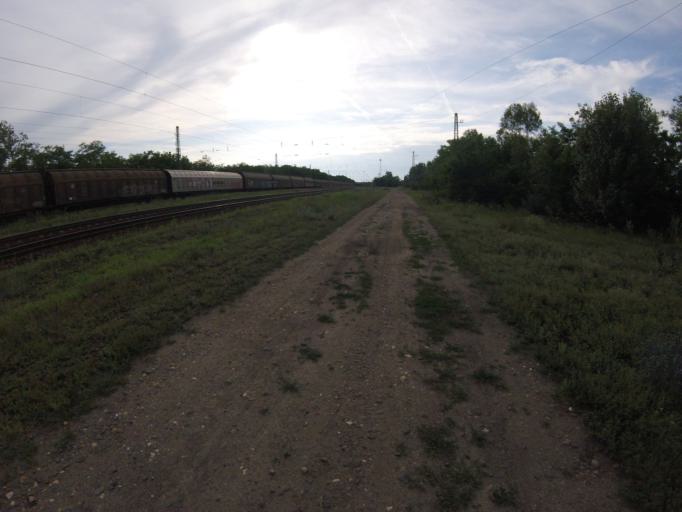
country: HU
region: Pest
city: Cegledbercel
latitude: 47.2093
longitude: 19.6906
